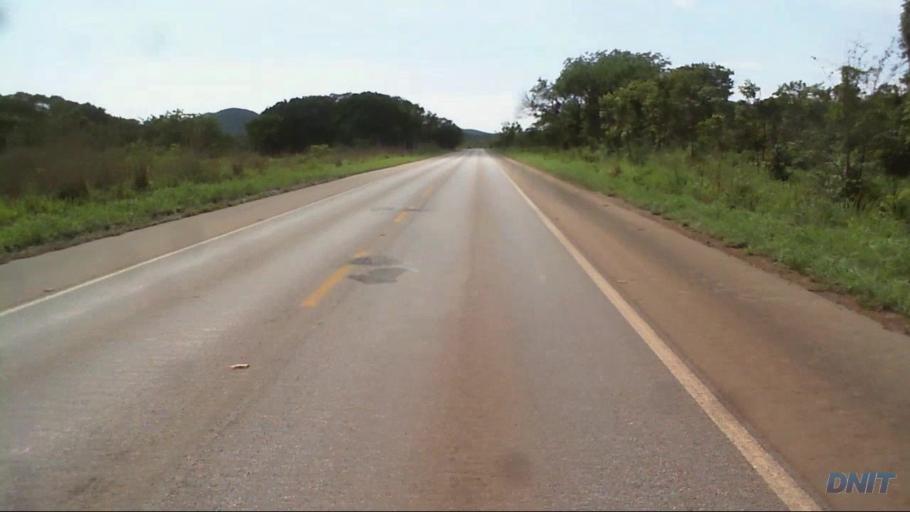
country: BR
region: Goias
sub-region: Barro Alto
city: Barro Alto
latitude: -15.1406
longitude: -48.8227
